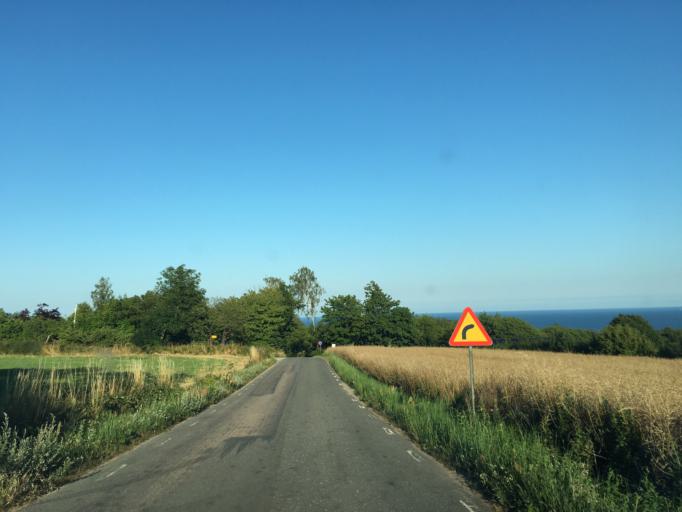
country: SE
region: Skane
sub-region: Simrishamns Kommun
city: Kivik
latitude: 55.6592
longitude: 14.2580
